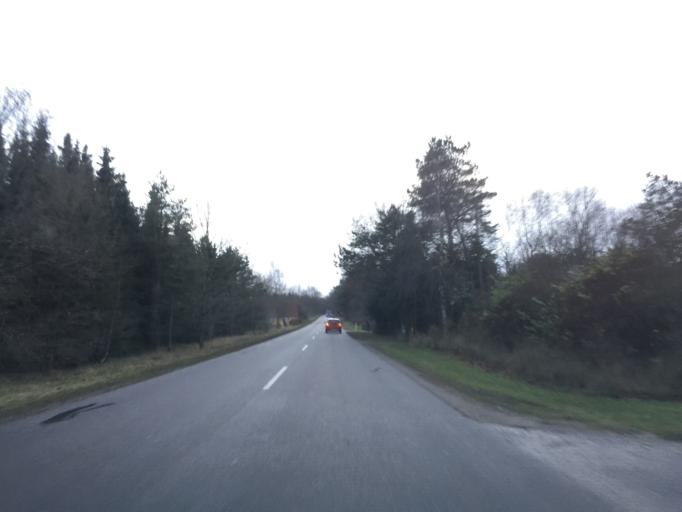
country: DK
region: Central Jutland
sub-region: Viborg Kommune
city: Bjerringbro
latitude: 56.3238
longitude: 9.6258
